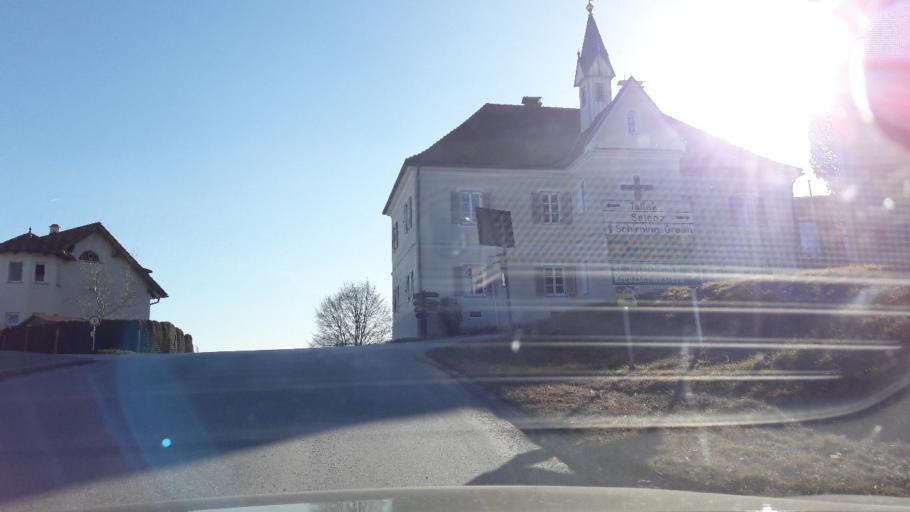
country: AT
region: Styria
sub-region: Politischer Bezirk Graz-Umgebung
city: Eisbach
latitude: 47.1324
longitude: 15.2874
